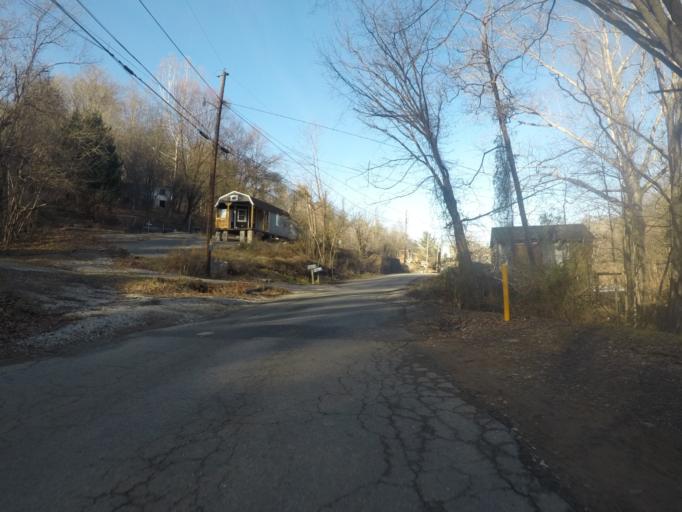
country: US
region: West Virginia
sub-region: Cabell County
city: Huntington
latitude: 38.3958
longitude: -82.4876
